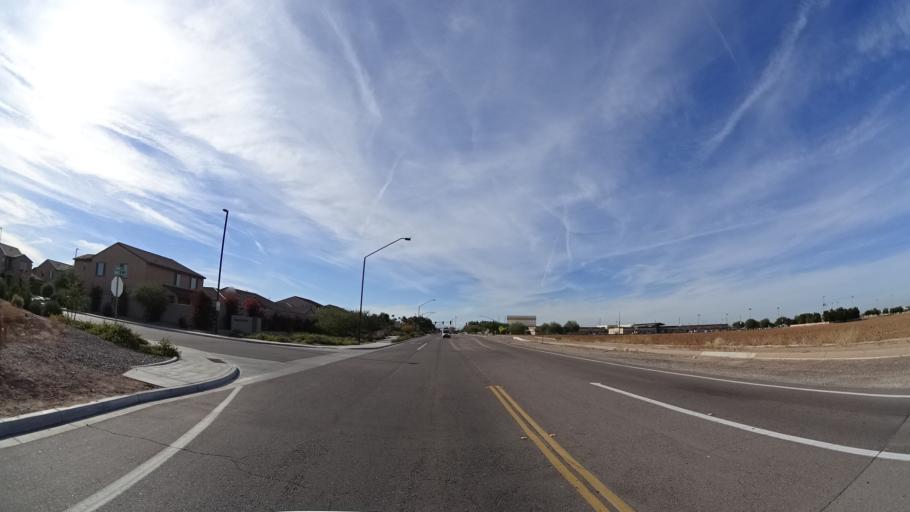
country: US
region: Arizona
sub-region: Maricopa County
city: Gilbert
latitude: 33.2772
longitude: -111.7572
